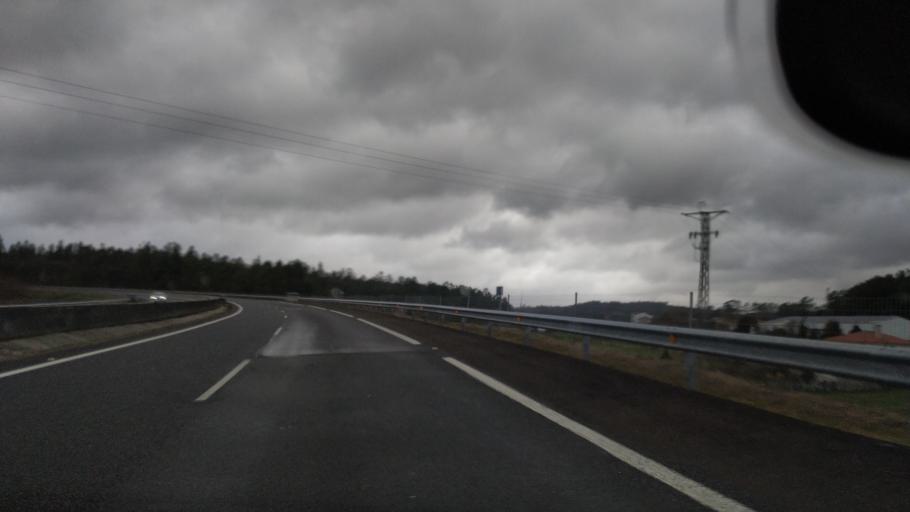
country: ES
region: Galicia
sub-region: Provincia da Coruna
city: Vedra
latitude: 42.8175
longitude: -8.4875
